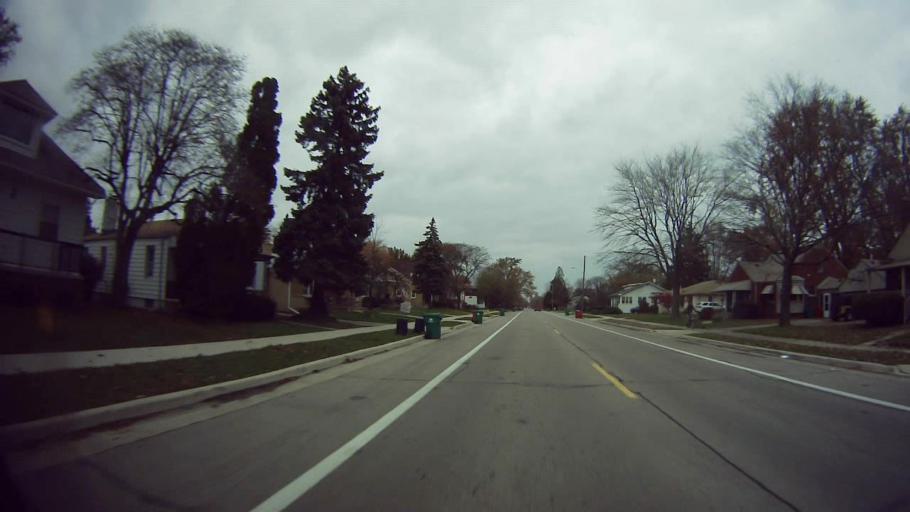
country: US
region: Michigan
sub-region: Macomb County
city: Eastpointe
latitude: 42.4657
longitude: -82.9666
